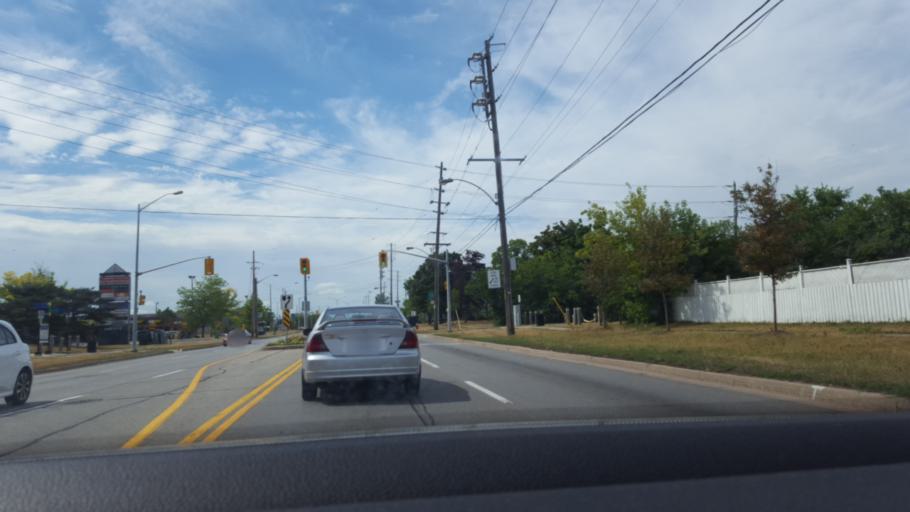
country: CA
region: Ontario
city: Burlington
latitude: 43.3720
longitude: -79.7599
